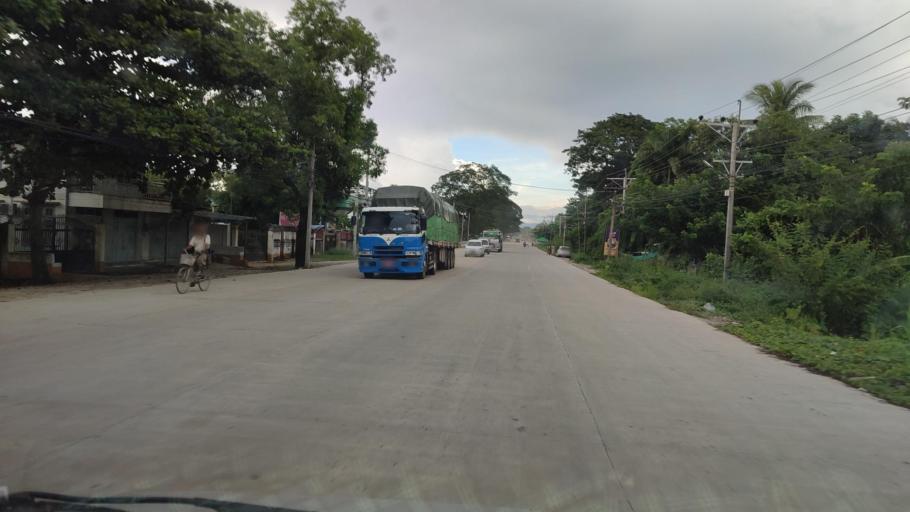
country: MM
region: Bago
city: Taungoo
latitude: 18.9053
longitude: 96.4393
